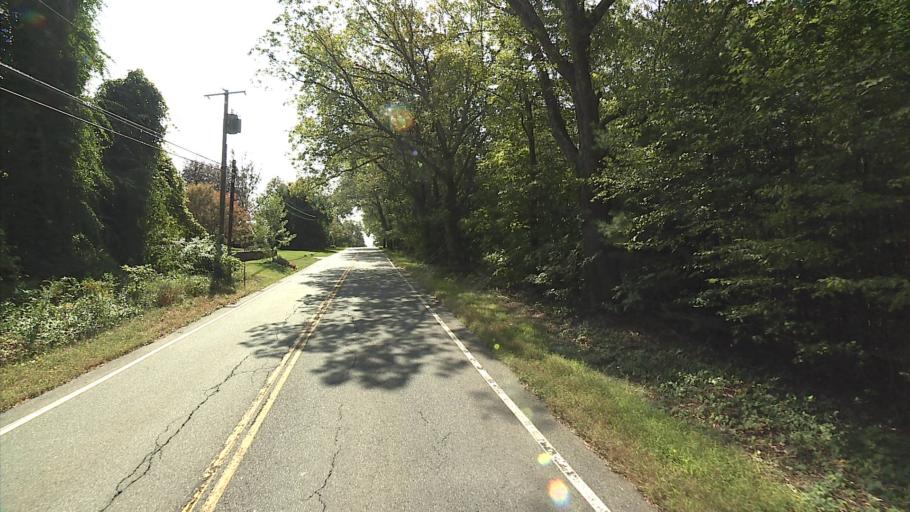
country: US
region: Connecticut
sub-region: Windham County
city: South Woodstock
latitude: 41.9735
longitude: -71.9906
